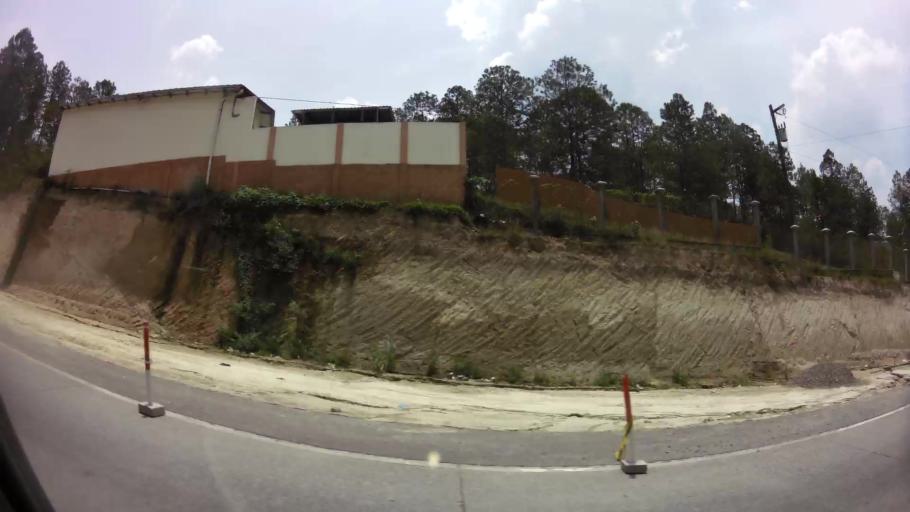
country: HN
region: Comayagua
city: El Socorro
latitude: 14.6341
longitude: -87.9218
